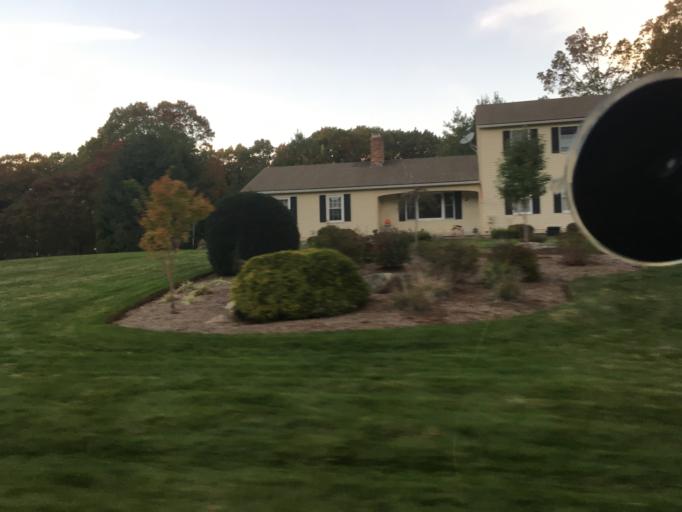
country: US
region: Rhode Island
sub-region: Kent County
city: West Warwick
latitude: 41.6503
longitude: -71.5124
